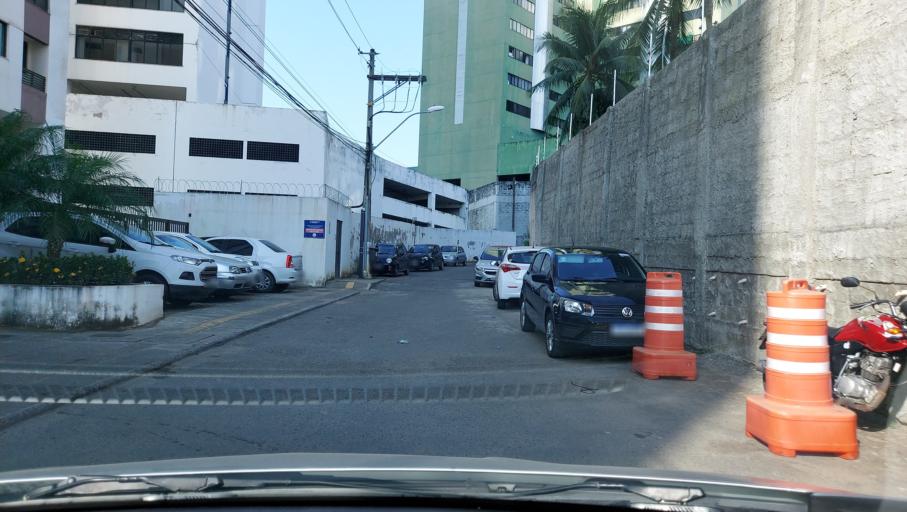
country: BR
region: Bahia
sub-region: Salvador
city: Salvador
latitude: -12.9851
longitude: -38.4687
